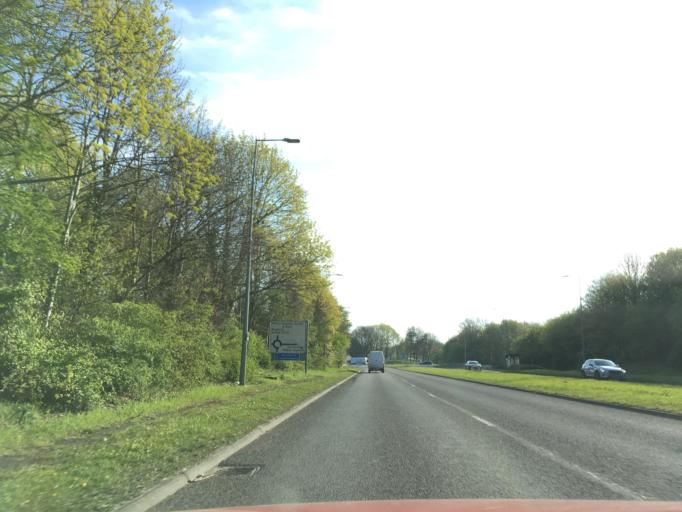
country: GB
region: England
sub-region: Milton Keynes
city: Bradwell
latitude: 52.0530
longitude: -0.7882
